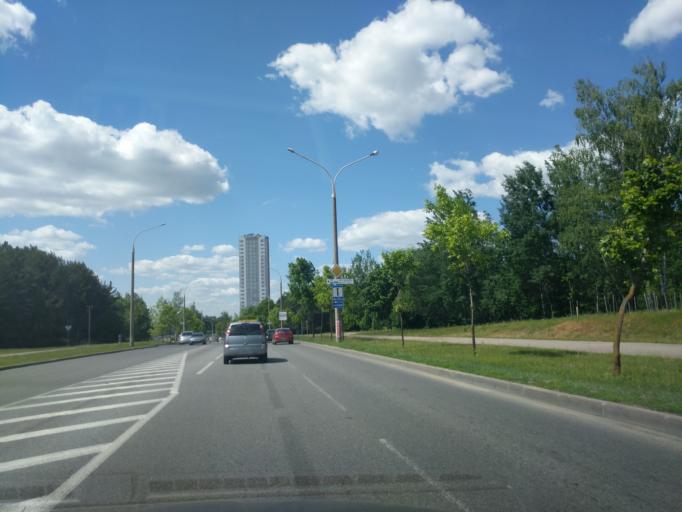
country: BY
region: Minsk
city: Borovlyany
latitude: 53.9262
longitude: 27.6604
